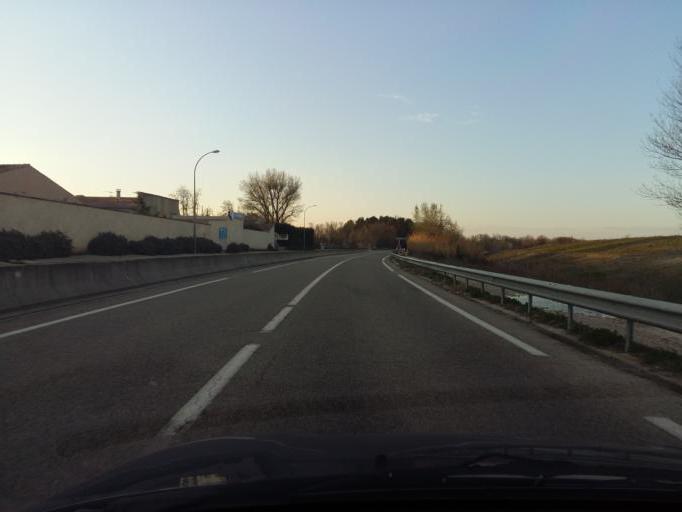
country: FR
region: Languedoc-Roussillon
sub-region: Departement du Gard
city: Roquemaure
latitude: 44.0514
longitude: 4.7846
